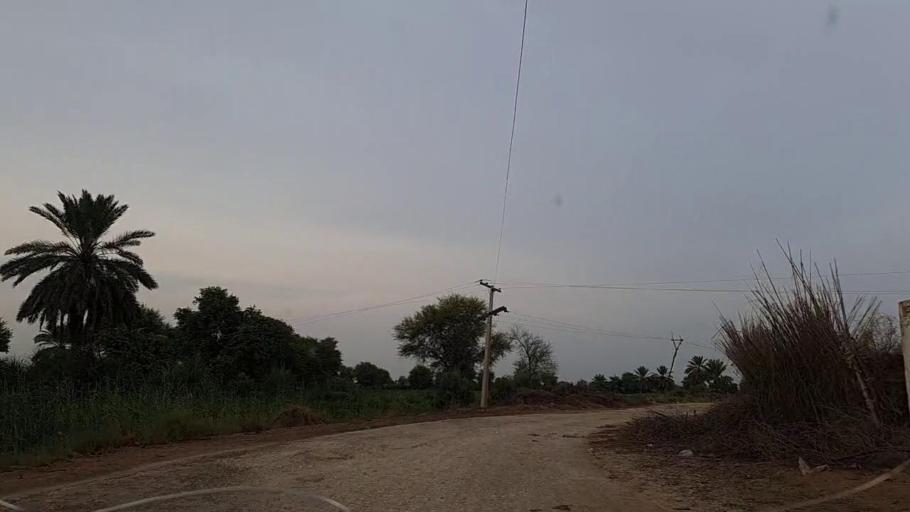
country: PK
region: Sindh
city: Mirpur Mathelo
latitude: 27.8714
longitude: 69.6344
